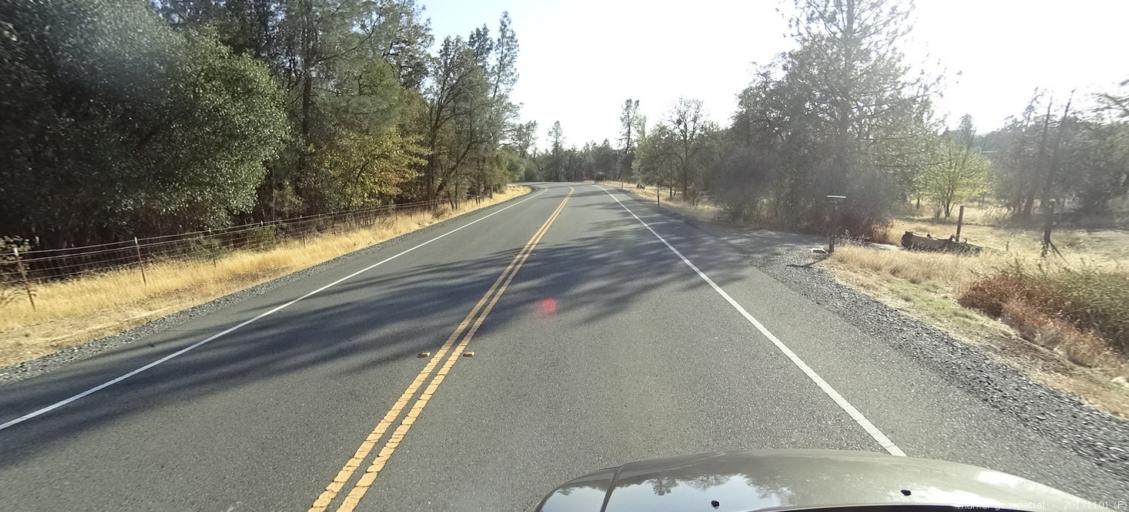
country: US
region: California
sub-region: Shasta County
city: Shasta Lake
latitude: 40.6434
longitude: -122.3292
